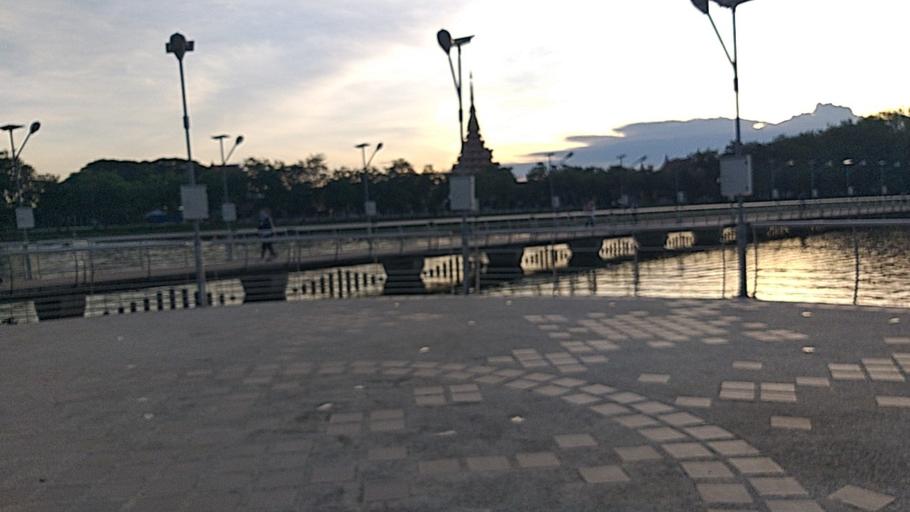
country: TH
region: Khon Kaen
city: Khon Kaen
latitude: 16.4081
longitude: 102.8374
